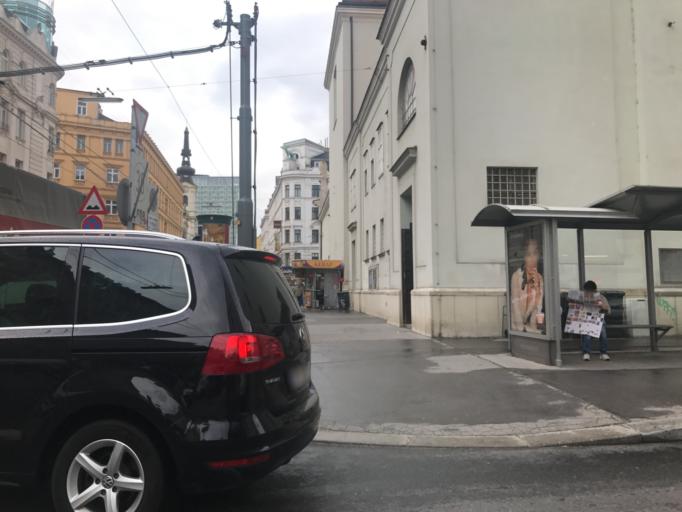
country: AT
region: Vienna
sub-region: Wien Stadt
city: Vienna
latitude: 48.2164
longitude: 16.3806
